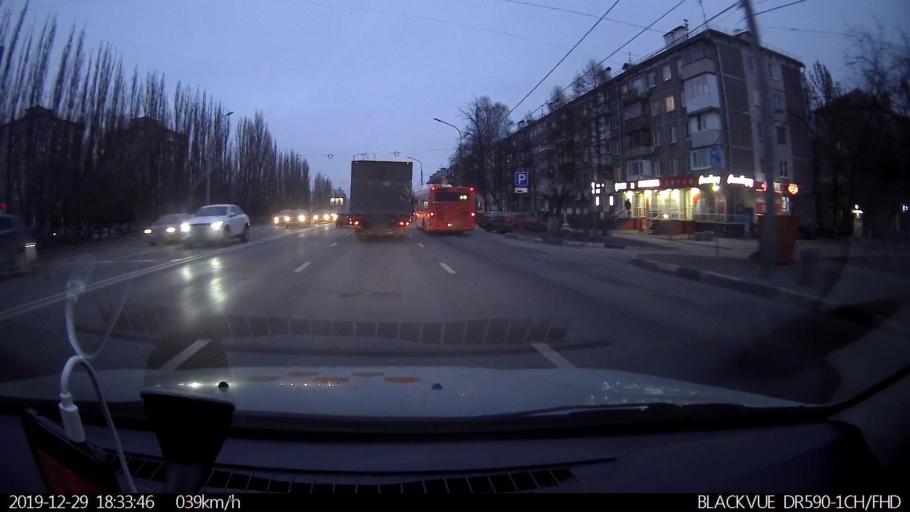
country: RU
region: Nizjnij Novgorod
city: Nizhniy Novgorod
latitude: 56.2815
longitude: 43.9254
